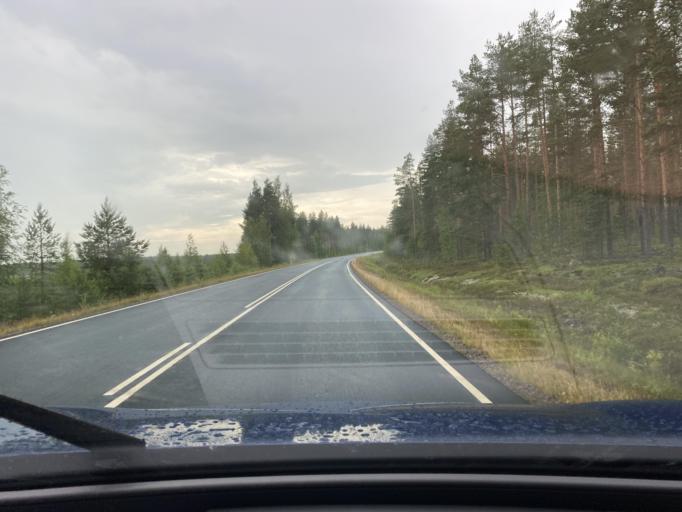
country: FI
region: Central Ostrobothnia
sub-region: Kaustinen
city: Veteli
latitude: 63.4107
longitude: 23.9604
